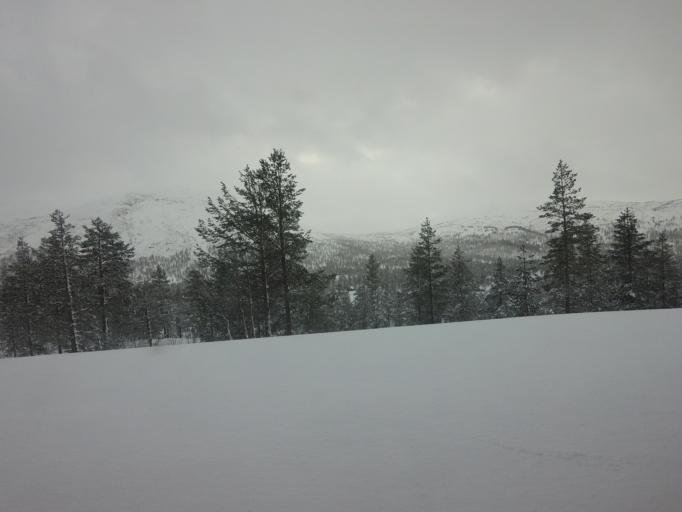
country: NO
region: Hordaland
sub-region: Ulvik
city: Ulvik
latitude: 60.6972
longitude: 6.8695
